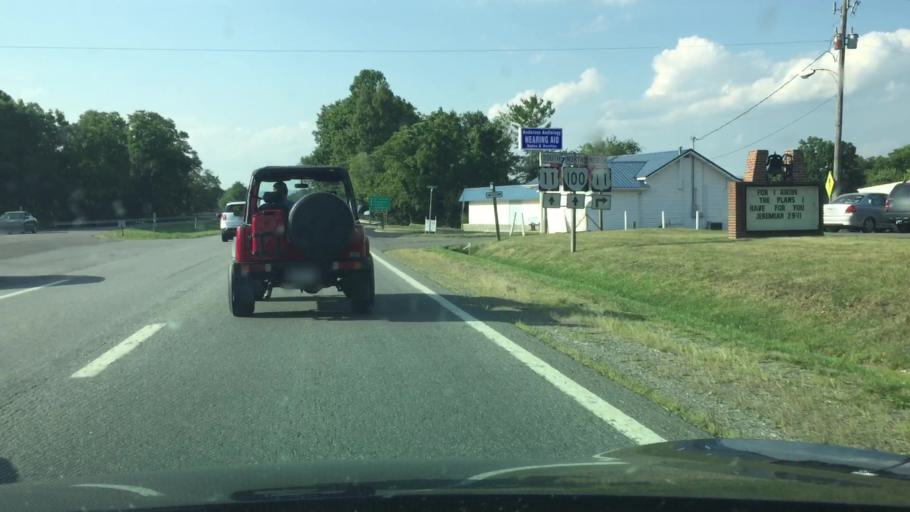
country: US
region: Virginia
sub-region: Pulaski County
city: Dublin
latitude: 37.0997
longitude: -80.6907
